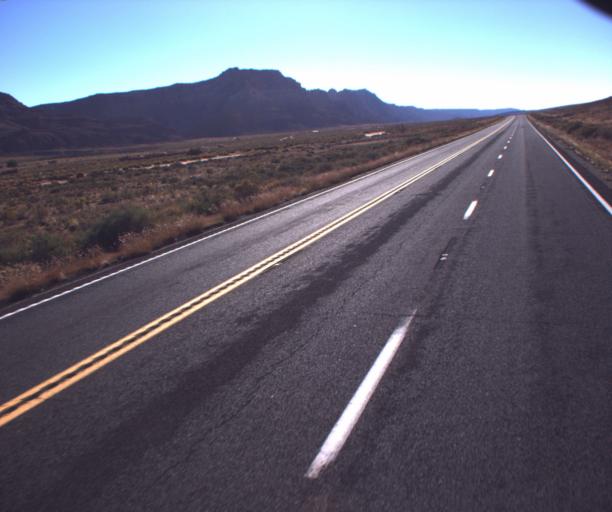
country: US
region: Arizona
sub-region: Coconino County
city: LeChee
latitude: 36.5840
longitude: -111.6492
